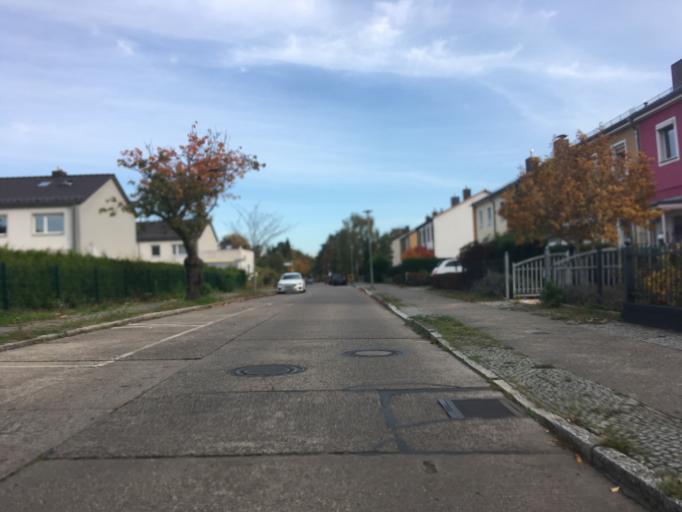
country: DE
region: Berlin
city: Zehlendorf Bezirk
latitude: 52.4212
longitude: 13.2379
